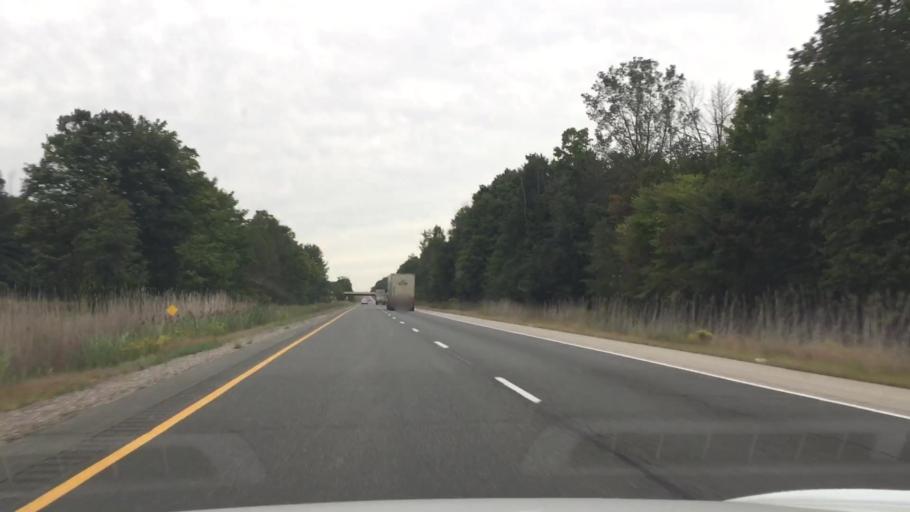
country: CA
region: Ontario
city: Lambton Shores
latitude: 42.9923
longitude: -81.7807
